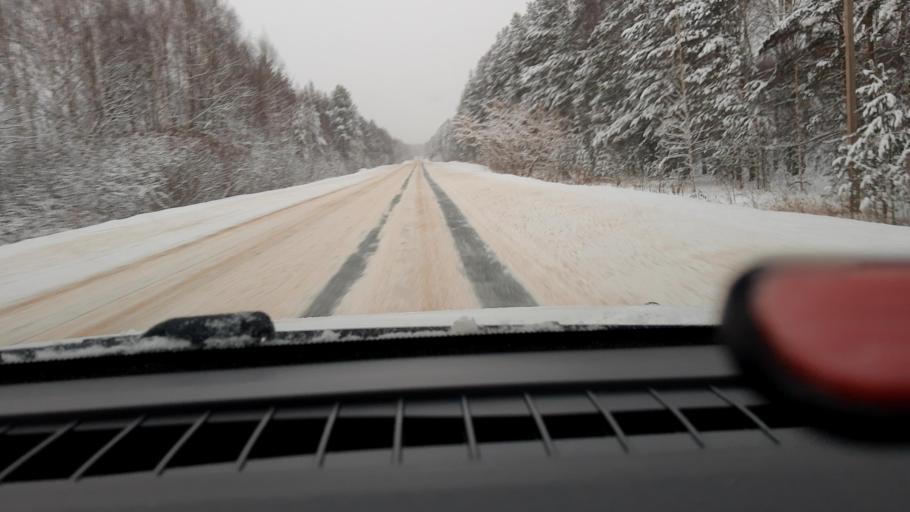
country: RU
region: Nizjnij Novgorod
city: Tonkino
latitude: 57.2859
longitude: 46.4618
